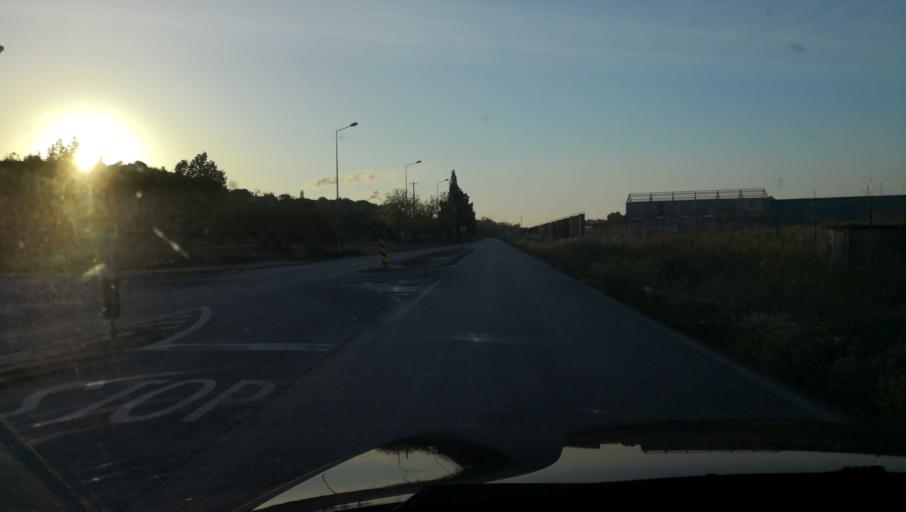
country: PT
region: Setubal
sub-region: Setubal
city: Setubal
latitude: 38.4931
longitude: -8.8279
